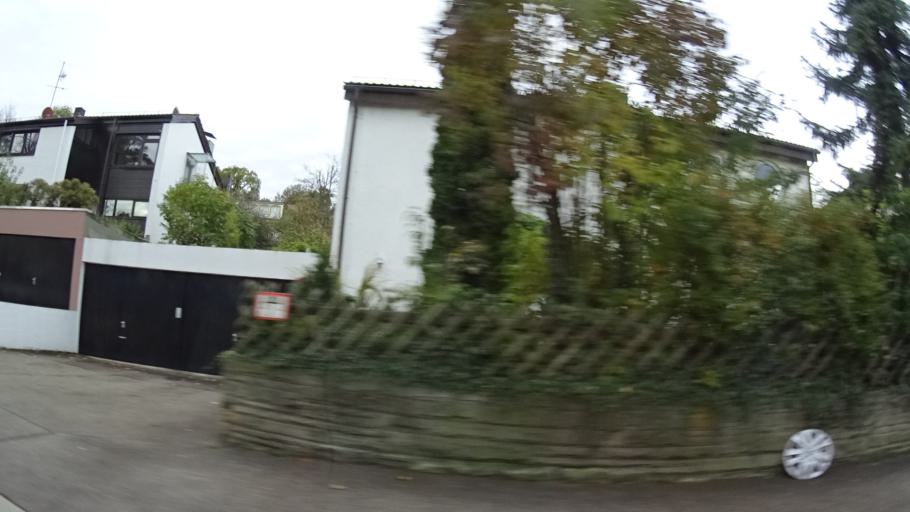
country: DE
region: Baden-Wuerttemberg
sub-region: Regierungsbezirk Stuttgart
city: Gerlingen
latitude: 48.7931
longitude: 9.0447
